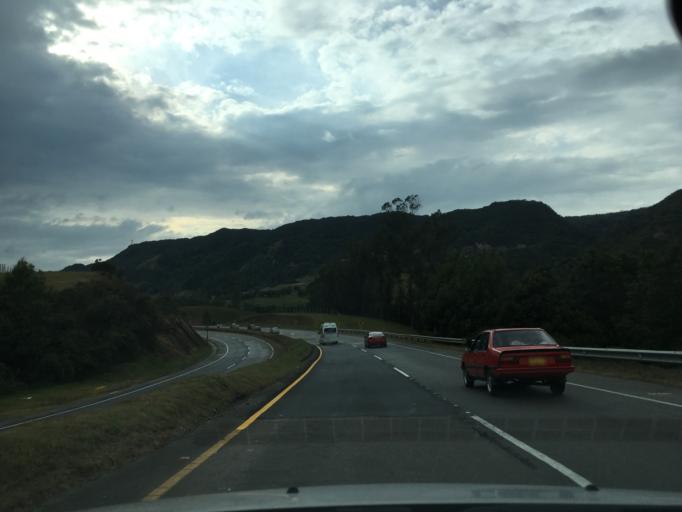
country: CO
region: Boyaca
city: Ventaquemada
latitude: 5.3974
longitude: -73.4915
